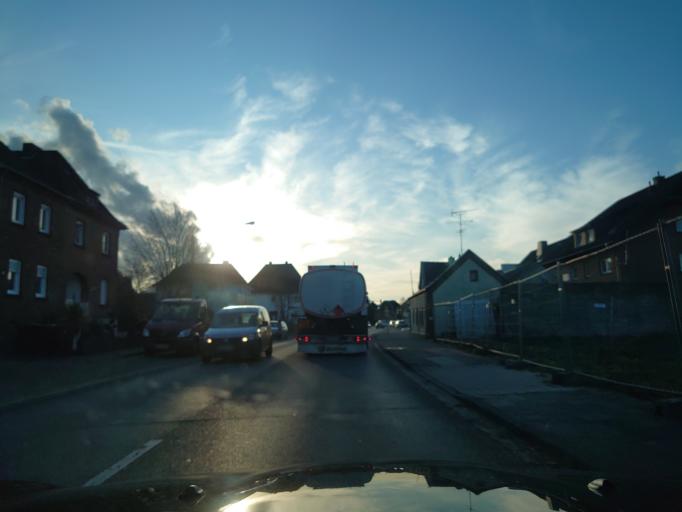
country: DE
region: North Rhine-Westphalia
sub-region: Regierungsbezirk Dusseldorf
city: Rommerskirchen
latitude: 51.0363
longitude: 6.6971
